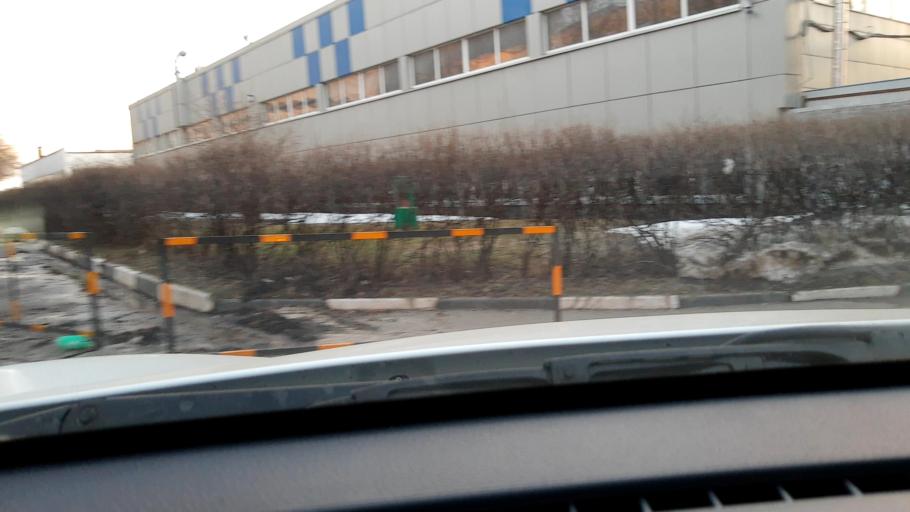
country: RU
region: Moscow
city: Tsaritsyno
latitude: 55.6160
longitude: 37.6230
